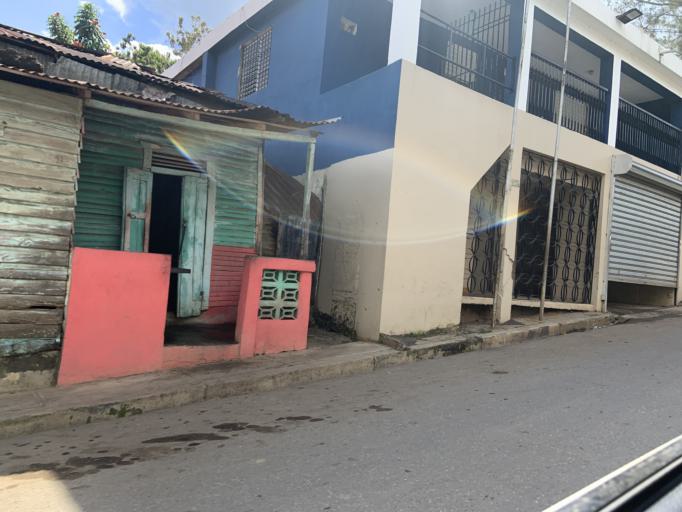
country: DO
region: Monte Plata
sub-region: Yamasa
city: Yamasa
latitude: 18.7718
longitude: -70.0276
